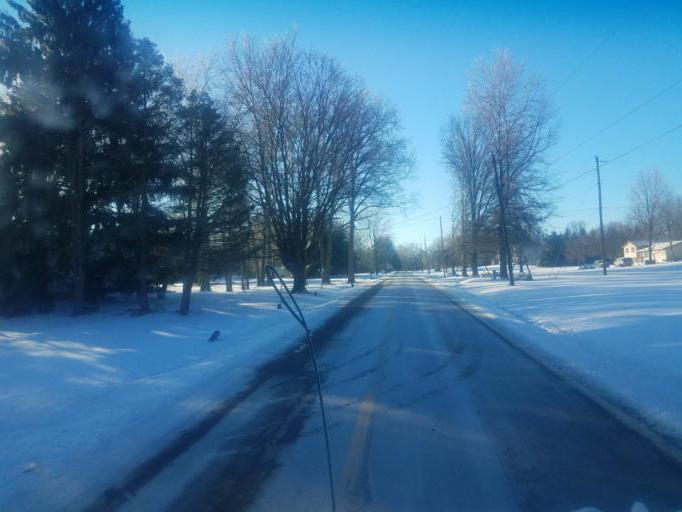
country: US
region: Ohio
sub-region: Delaware County
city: Sunbury
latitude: 40.2116
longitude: -82.9134
